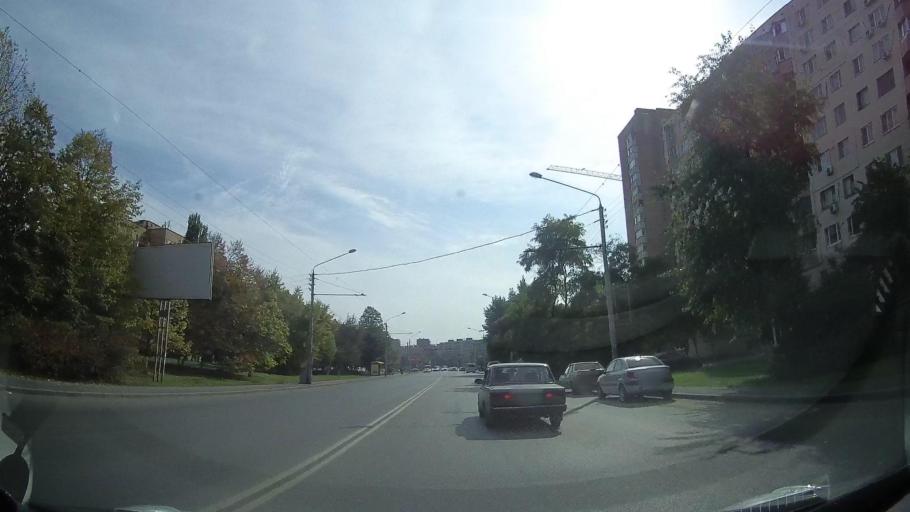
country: RU
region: Rostov
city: Severnyy
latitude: 47.2907
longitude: 39.7035
